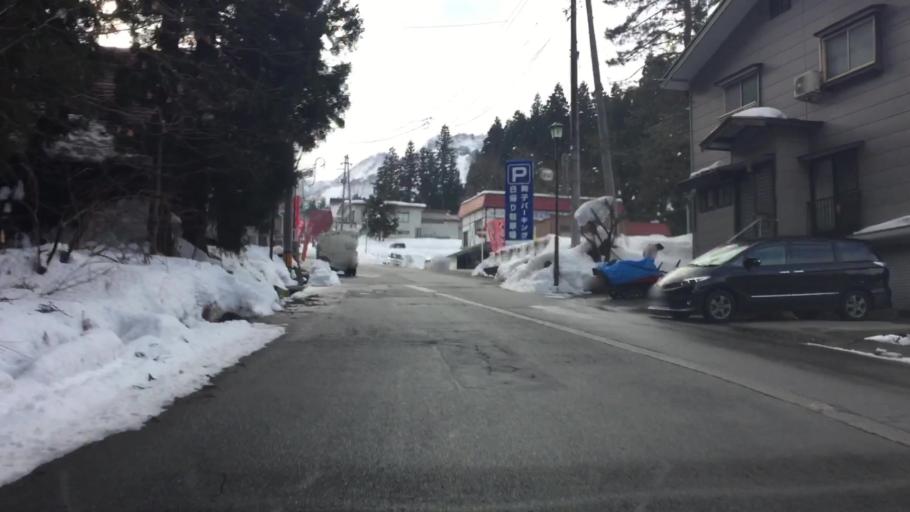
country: JP
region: Niigata
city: Shiozawa
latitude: 36.9877
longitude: 138.8220
